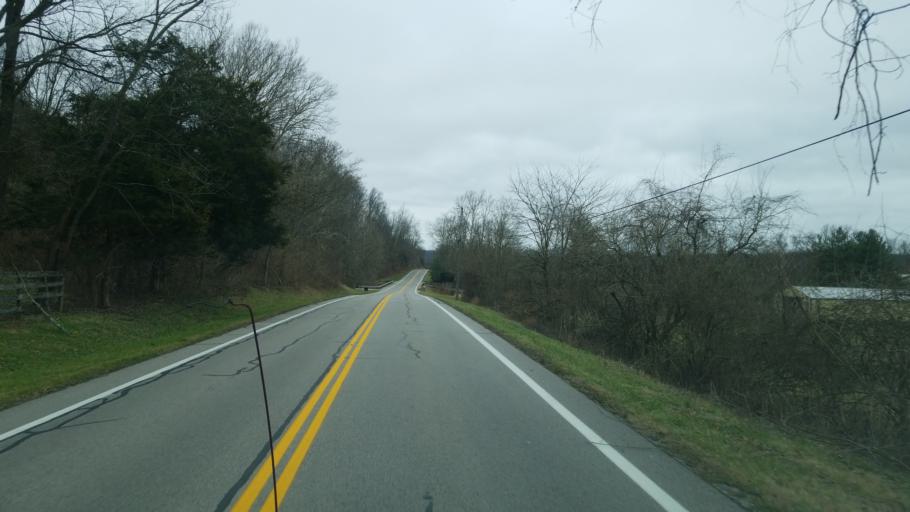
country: US
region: Ohio
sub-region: Clermont County
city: New Richmond
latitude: 38.8346
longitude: -84.2210
